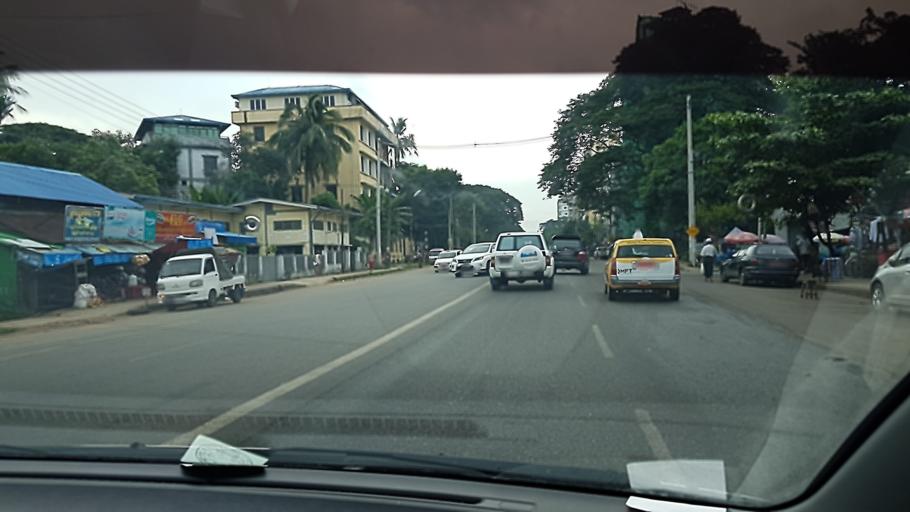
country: MM
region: Yangon
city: Yangon
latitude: 16.7937
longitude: 96.1265
